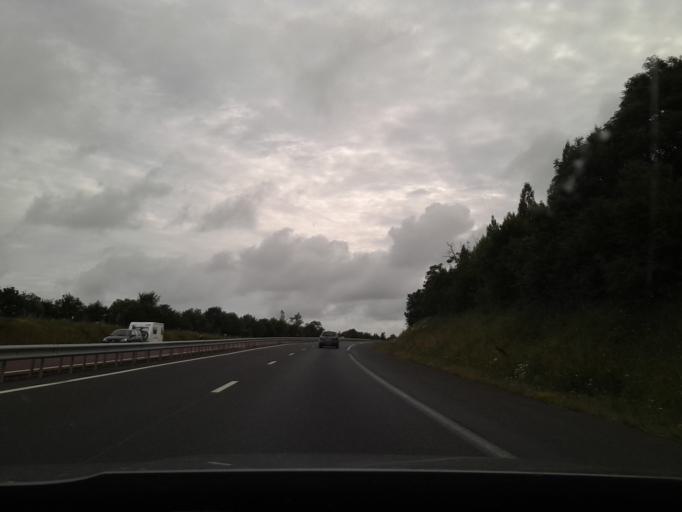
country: FR
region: Lower Normandy
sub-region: Departement du Calvados
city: Isigny-sur-Mer
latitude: 49.3384
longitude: -1.0597
